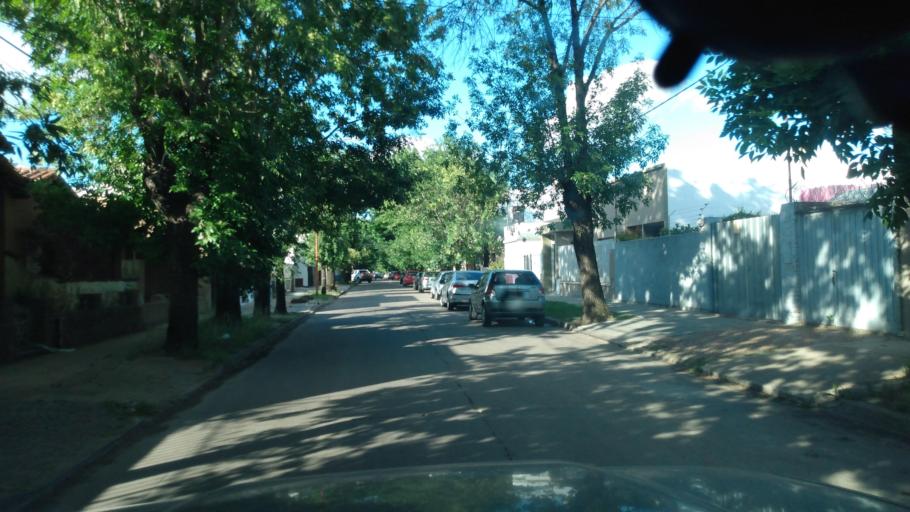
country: AR
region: Buenos Aires
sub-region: Partido de Lujan
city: Lujan
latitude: -34.5676
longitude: -59.1078
